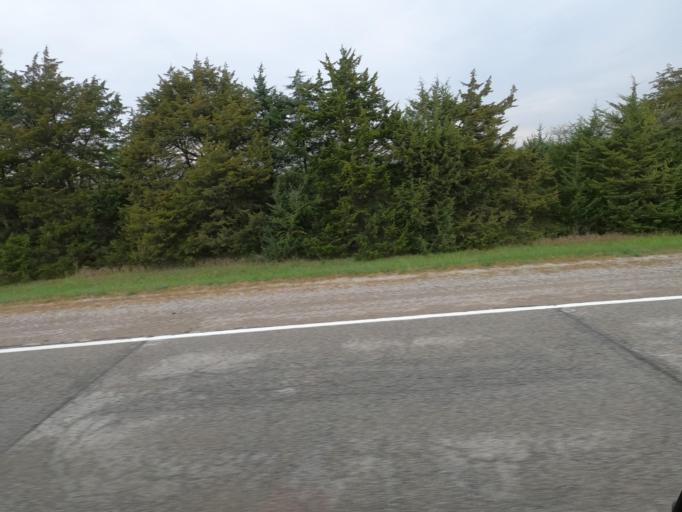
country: US
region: Iowa
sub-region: Van Buren County
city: Keosauqua
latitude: 40.8347
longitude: -91.9910
